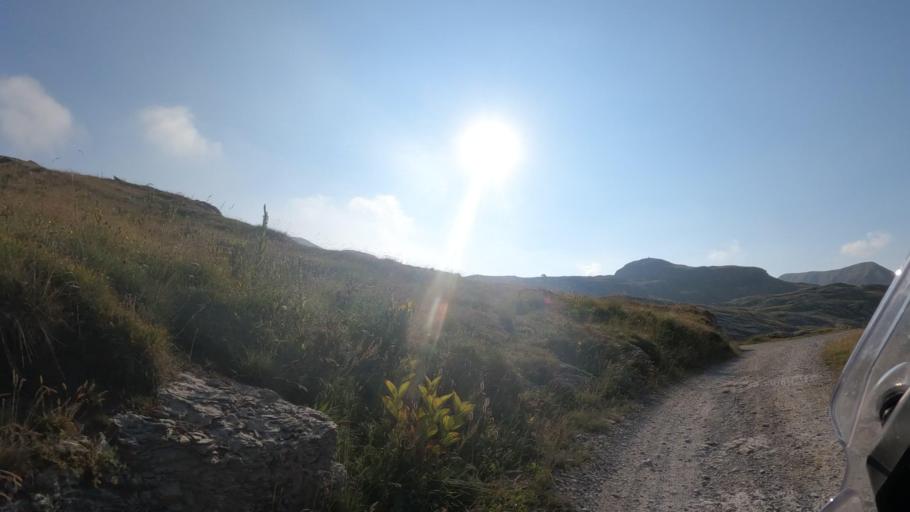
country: IT
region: Piedmont
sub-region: Provincia di Cuneo
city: Limone Piemonte
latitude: 44.1738
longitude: 7.6373
